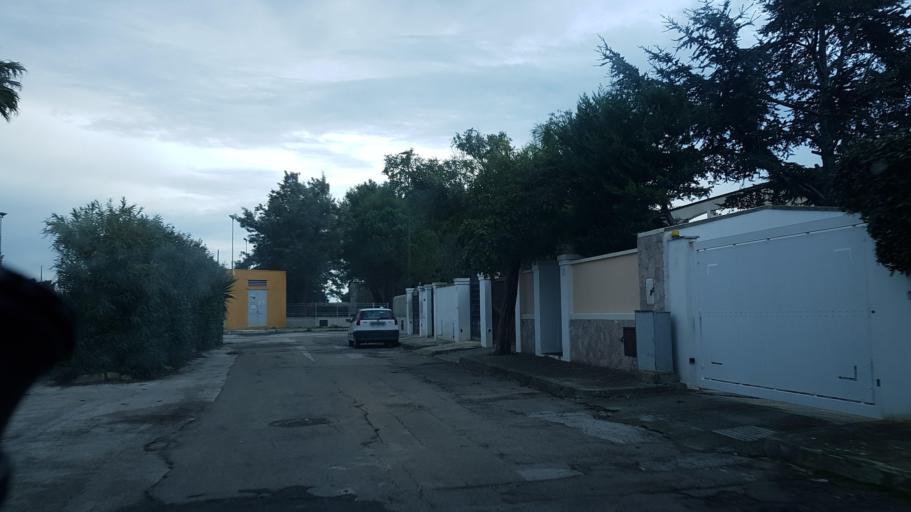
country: IT
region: Apulia
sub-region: Provincia di Lecce
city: Merine
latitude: 40.3378
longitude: 18.2185
